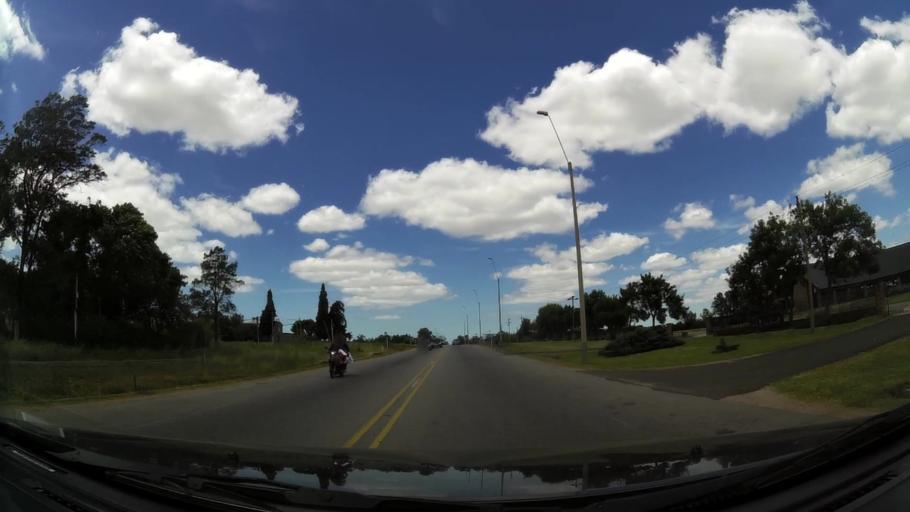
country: UY
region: Canelones
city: Colonia Nicolich
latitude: -34.8032
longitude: -56.0050
